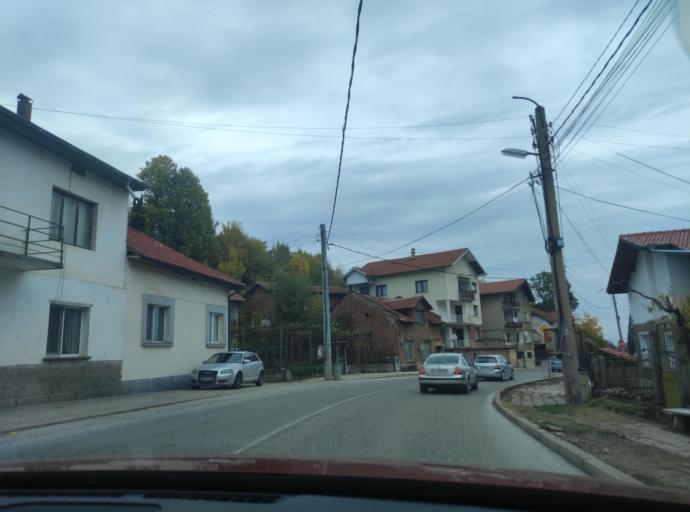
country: BG
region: Montana
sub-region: Obshtina Berkovitsa
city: Berkovitsa
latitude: 43.1962
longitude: 23.1606
